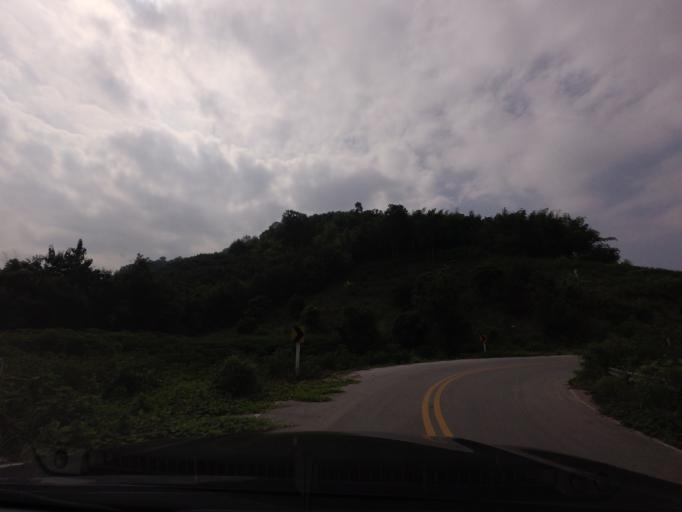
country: LA
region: Xiagnabouli
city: Muang Kenthao
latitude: 17.7654
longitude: 101.5143
